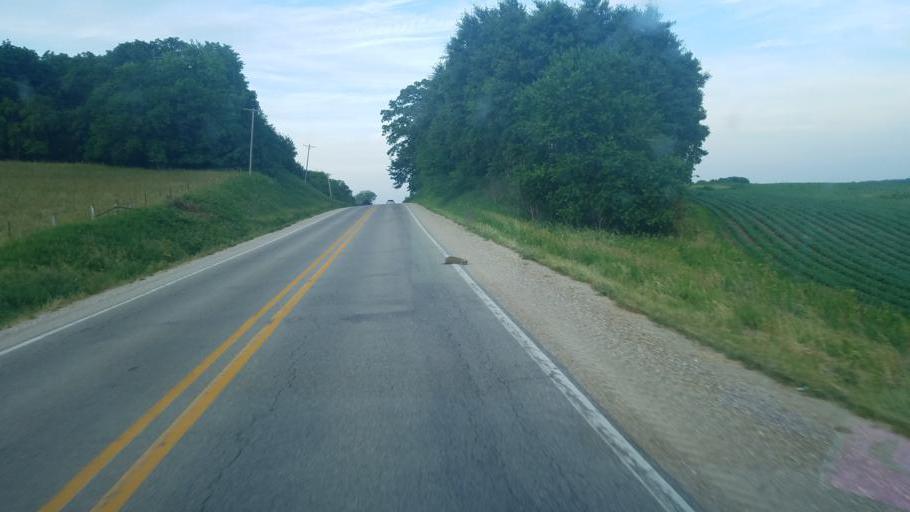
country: US
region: Iowa
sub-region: Benton County
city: Belle Plaine
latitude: 41.9060
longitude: -92.3284
